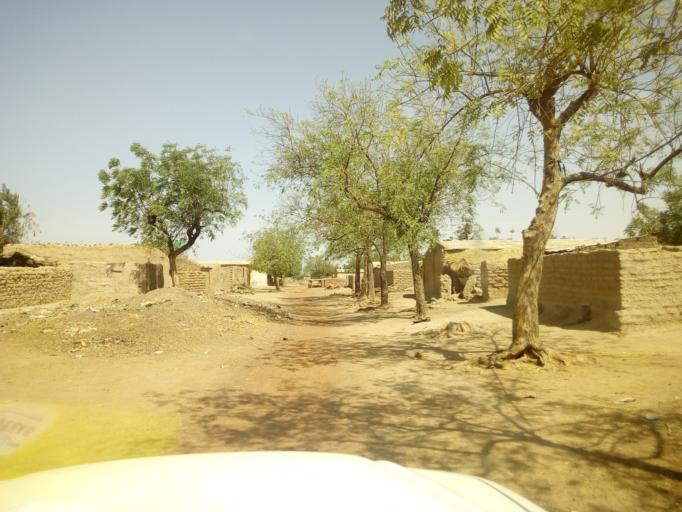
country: ML
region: Koulikoro
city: Koulikoro
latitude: 12.6486
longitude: -7.7102
